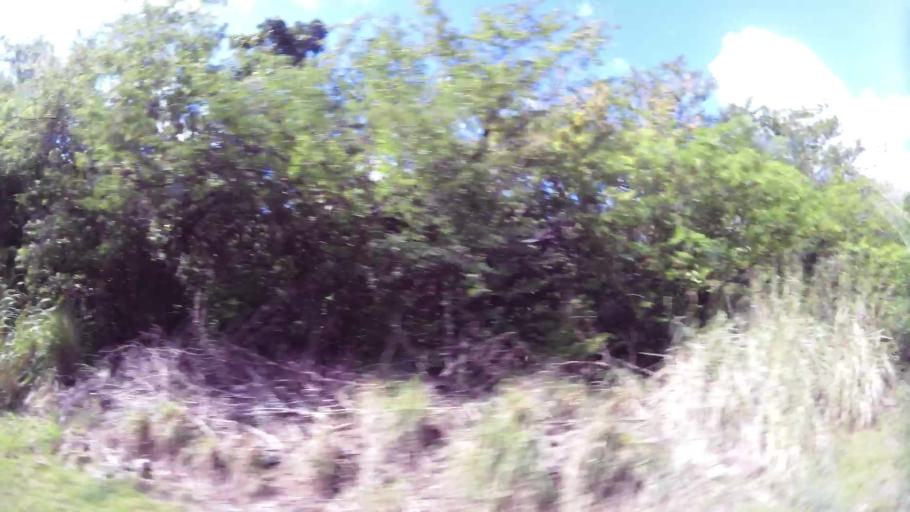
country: DM
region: Saint John
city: Portsmouth
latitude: 15.5894
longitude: -61.4638
